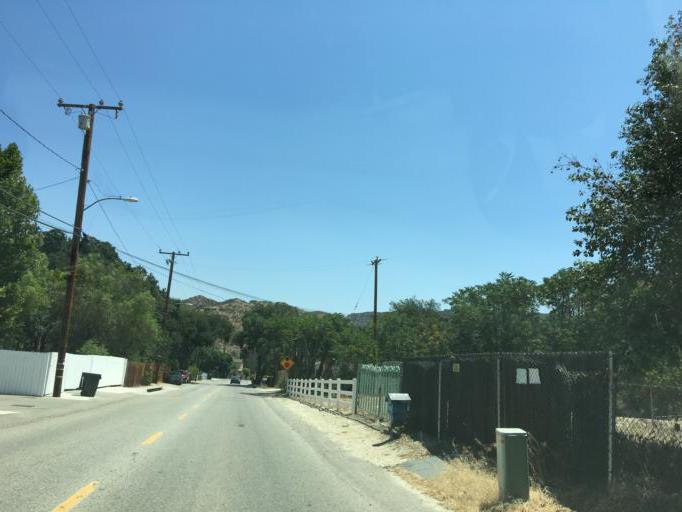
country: US
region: California
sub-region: Los Angeles County
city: Val Verde
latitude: 34.4456
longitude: -118.6598
